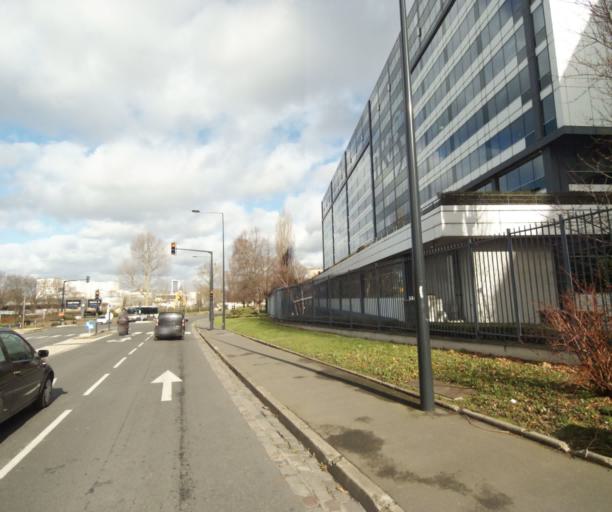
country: FR
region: Ile-de-France
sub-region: Departement de Seine-Saint-Denis
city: Saint-Denis
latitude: 48.9291
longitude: 2.3411
